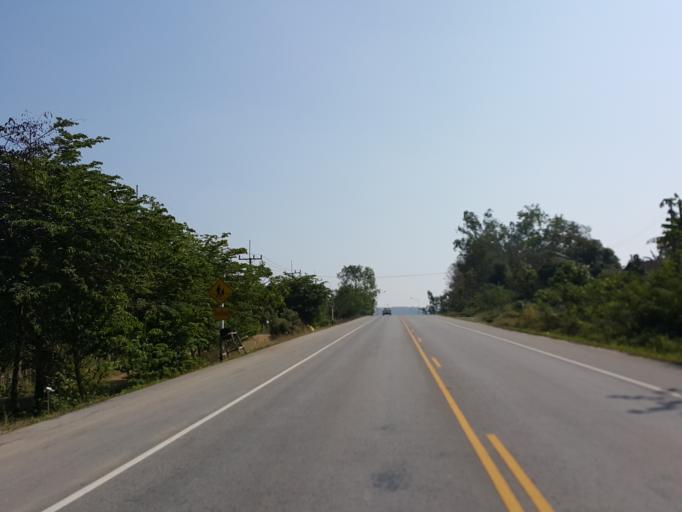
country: TH
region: Lampang
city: Wang Nuea
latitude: 18.9953
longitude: 99.6141
